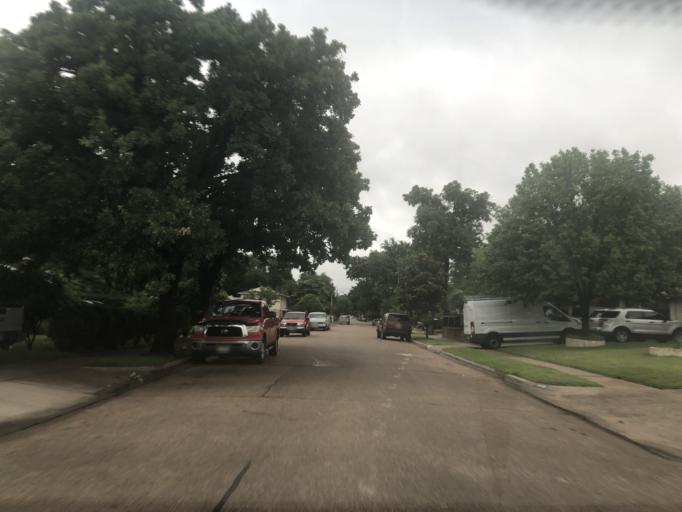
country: US
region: Texas
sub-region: Dallas County
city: Irving
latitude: 32.7947
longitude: -96.9497
